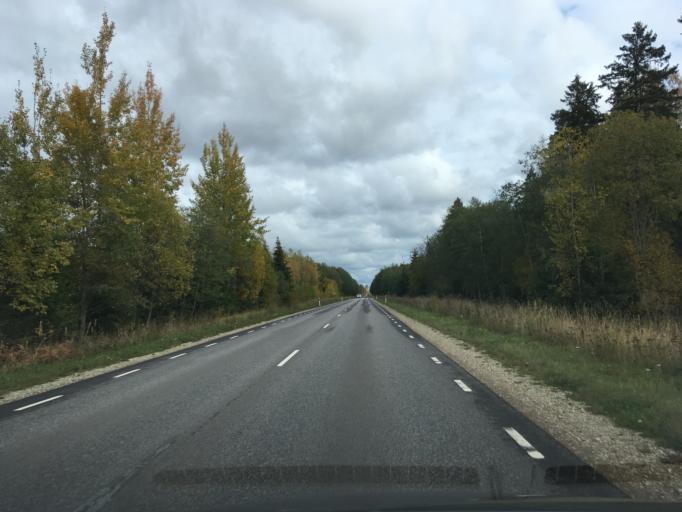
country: EE
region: Harju
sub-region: Anija vald
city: Kehra
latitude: 59.2379
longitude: 25.2908
